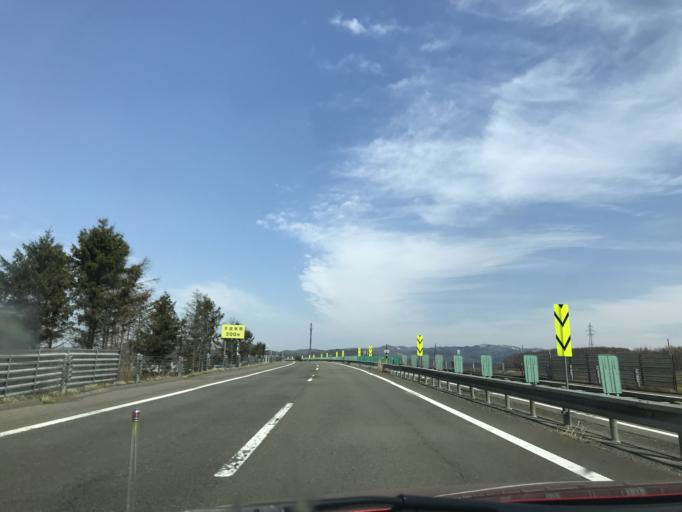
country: JP
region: Hokkaido
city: Iwamizawa
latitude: 43.2212
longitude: 141.8282
